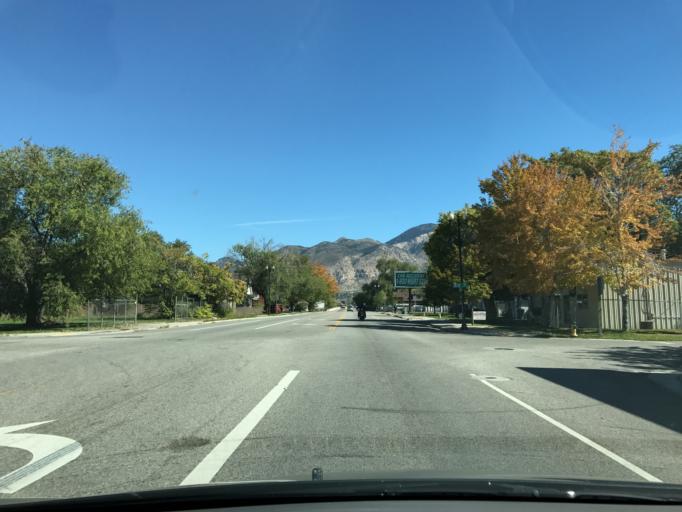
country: US
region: Utah
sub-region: Weber County
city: Ogden
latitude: 41.2230
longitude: -111.9916
